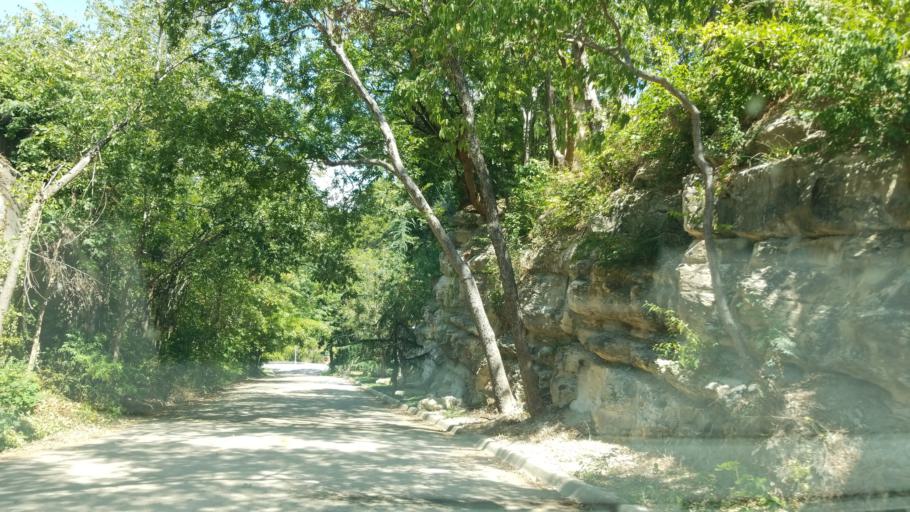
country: US
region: Texas
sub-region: Dallas County
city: Dallas
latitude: 32.7658
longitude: -96.8313
